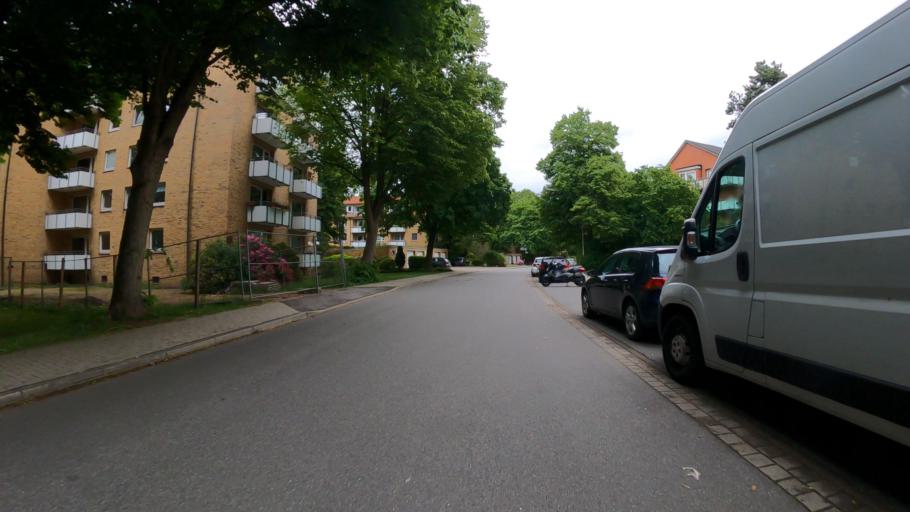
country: DE
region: Schleswig-Holstein
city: Norderstedt
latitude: 53.6852
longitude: 9.9909
